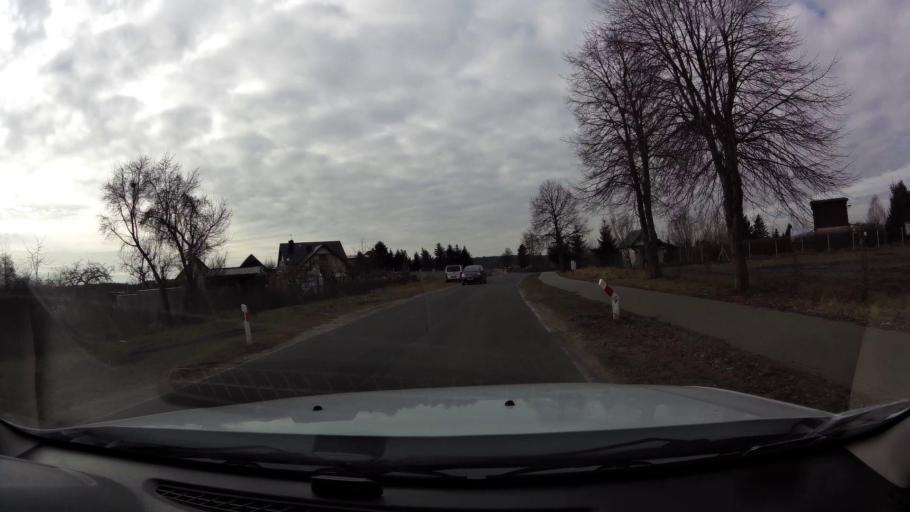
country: PL
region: West Pomeranian Voivodeship
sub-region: Powiat mysliborski
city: Debno
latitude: 52.7305
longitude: 14.6901
